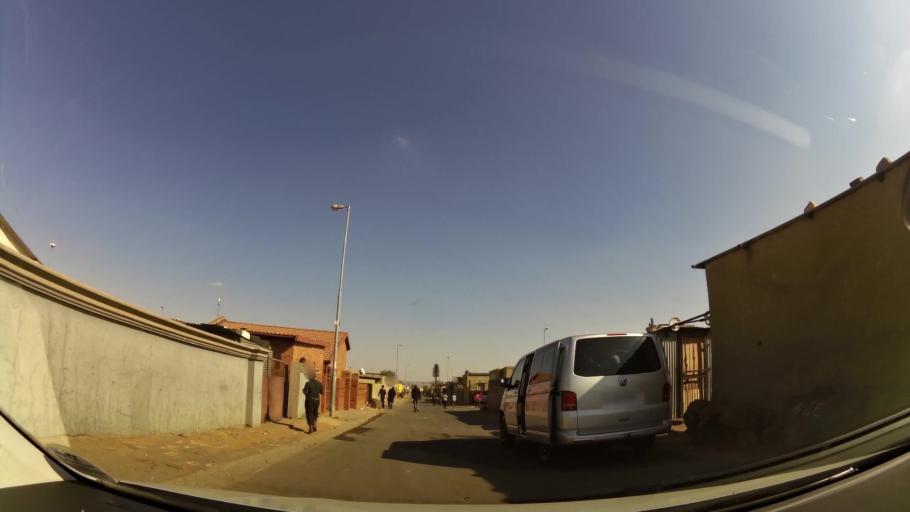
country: ZA
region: Gauteng
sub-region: City of Johannesburg Metropolitan Municipality
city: Soweto
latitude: -26.2839
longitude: 27.8693
